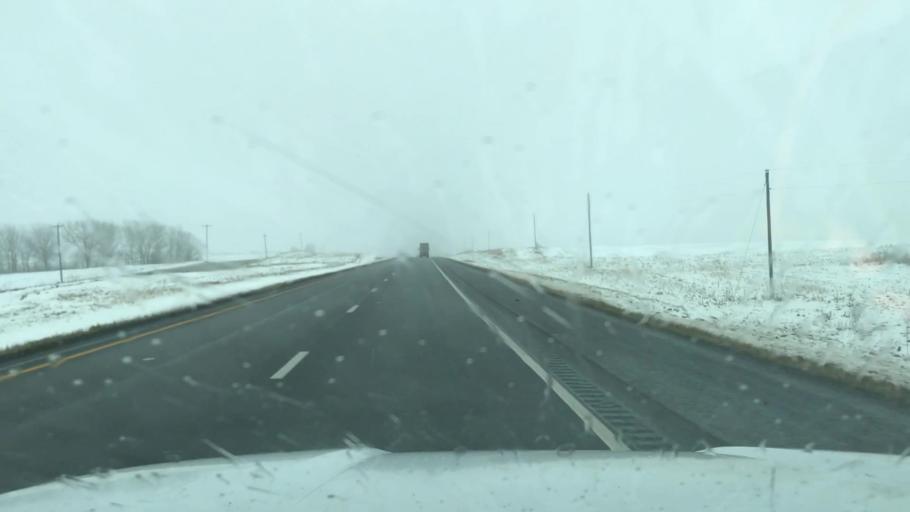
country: US
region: Missouri
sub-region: Clinton County
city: Gower
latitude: 39.7620
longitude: -94.5258
